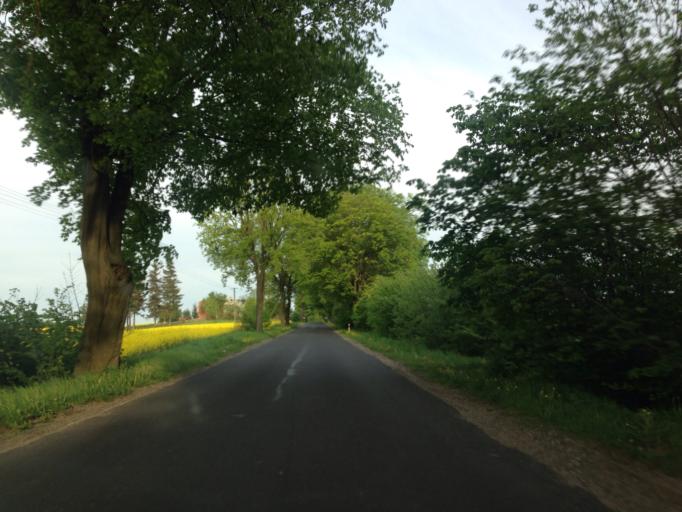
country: PL
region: Kujawsko-Pomorskie
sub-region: Powiat wabrzeski
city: Debowa Laka
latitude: 53.2548
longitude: 19.1087
